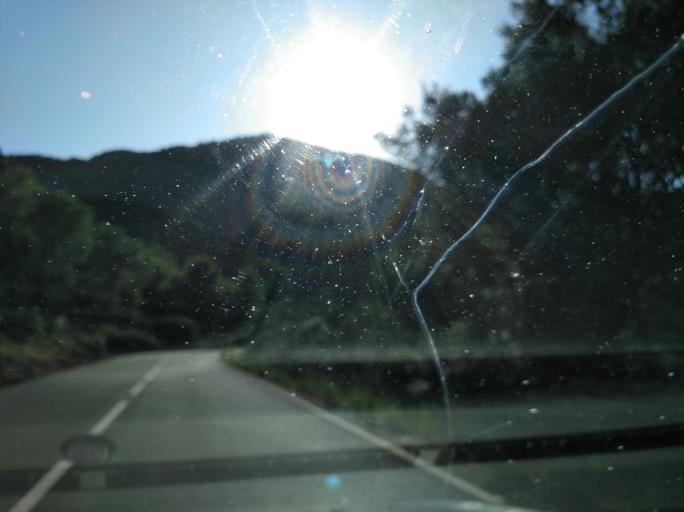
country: ES
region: Catalonia
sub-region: Provincia de Girona
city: Llanca
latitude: 42.3541
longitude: 3.1702
